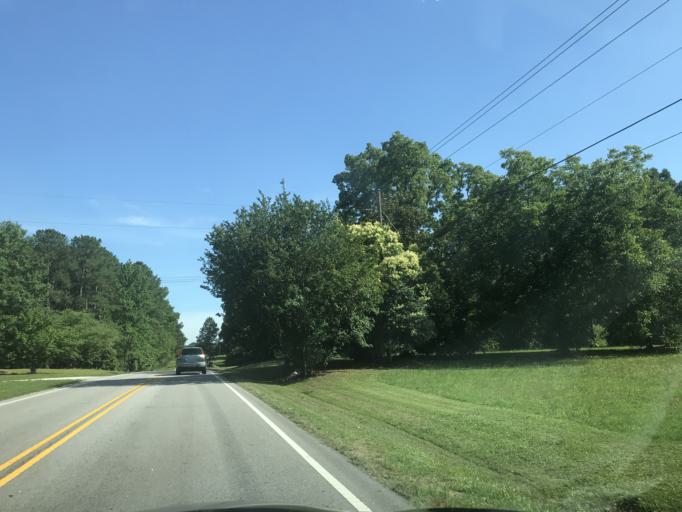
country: US
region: North Carolina
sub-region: Wake County
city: Garner
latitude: 35.6775
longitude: -78.5777
